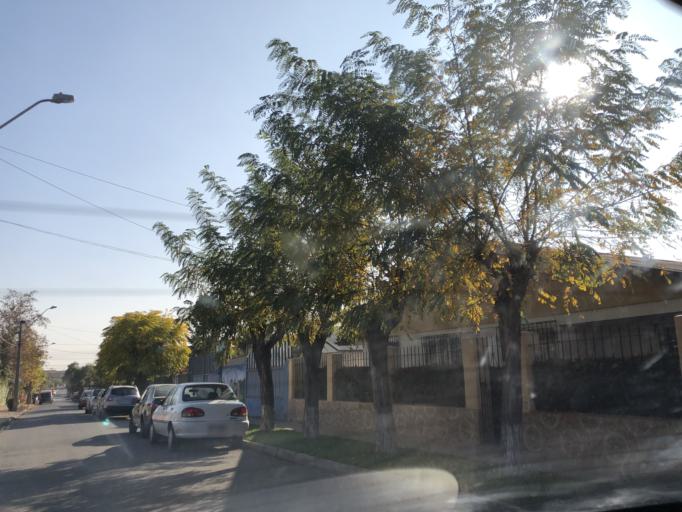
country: CL
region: Santiago Metropolitan
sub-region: Provincia de Cordillera
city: Puente Alto
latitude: -33.6248
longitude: -70.5855
